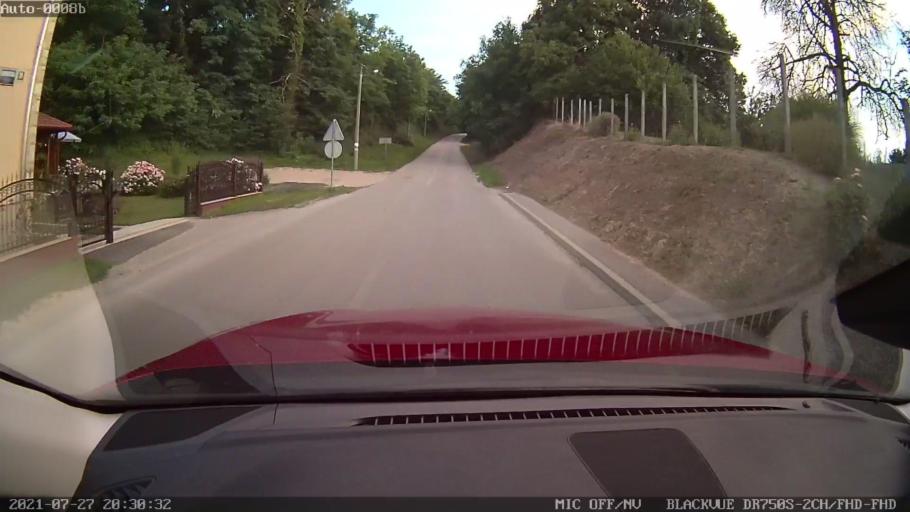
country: HR
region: Varazdinska
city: Jalzabet
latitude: 46.2542
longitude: 16.4728
